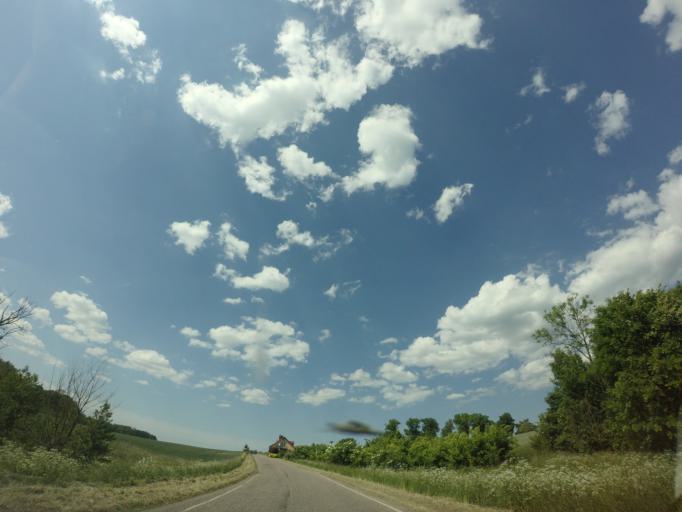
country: PL
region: West Pomeranian Voivodeship
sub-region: Powiat stargardzki
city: Dolice
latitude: 53.1563
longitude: 15.2397
